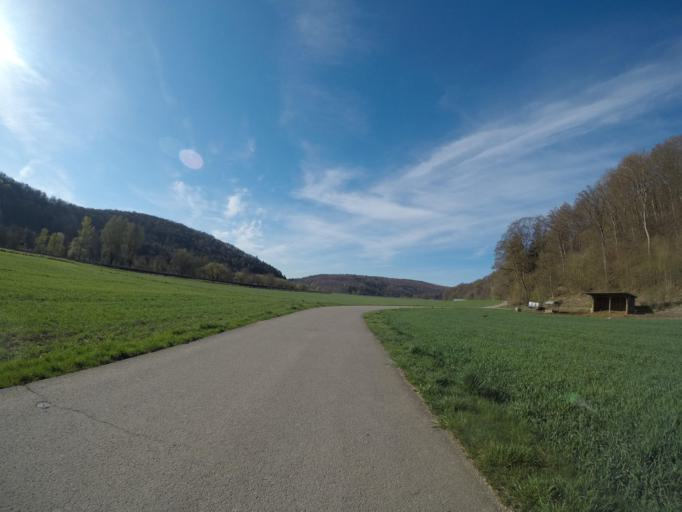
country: DE
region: Baden-Wuerttemberg
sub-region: Tuebingen Region
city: Allmendingen
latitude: 48.3553
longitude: 9.7133
